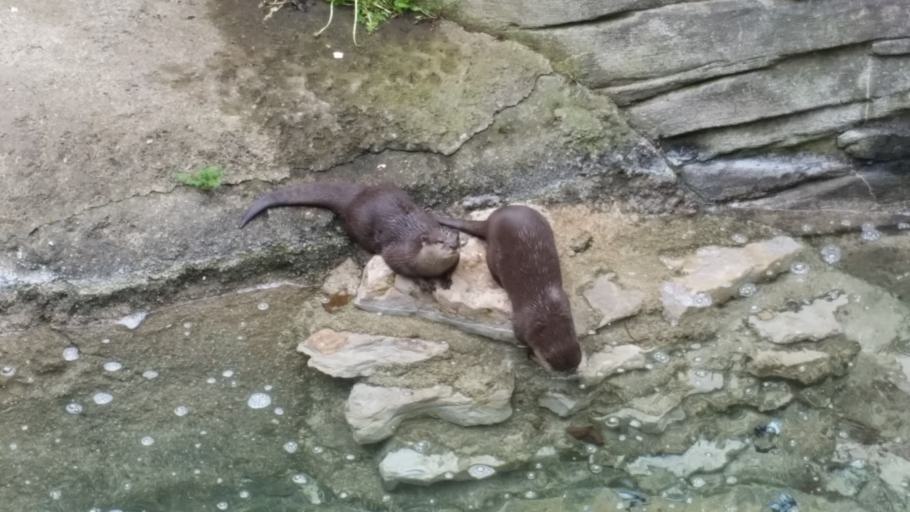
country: US
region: Ohio
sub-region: Delaware County
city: Powell
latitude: 40.1507
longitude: -83.1270
